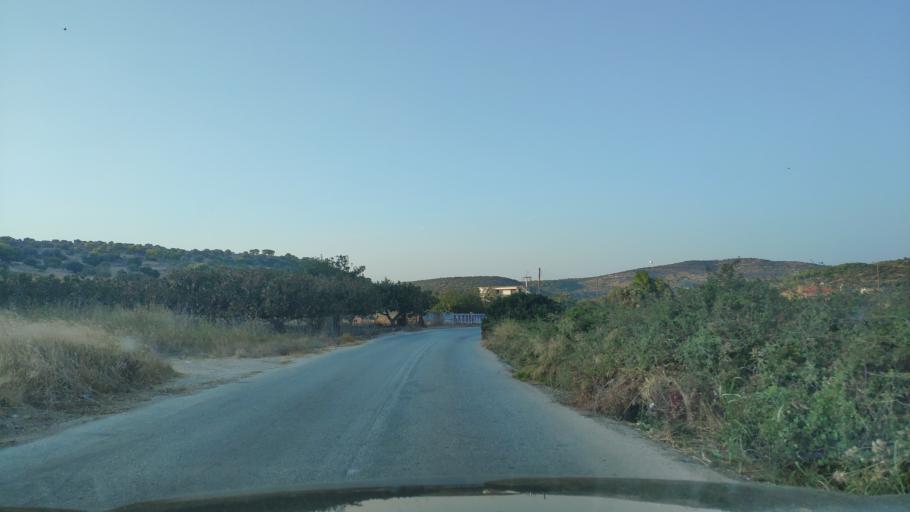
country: GR
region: Attica
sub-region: Nomarchia Anatolikis Attikis
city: Limin Mesoyaias
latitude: 37.9224
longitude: 23.9774
